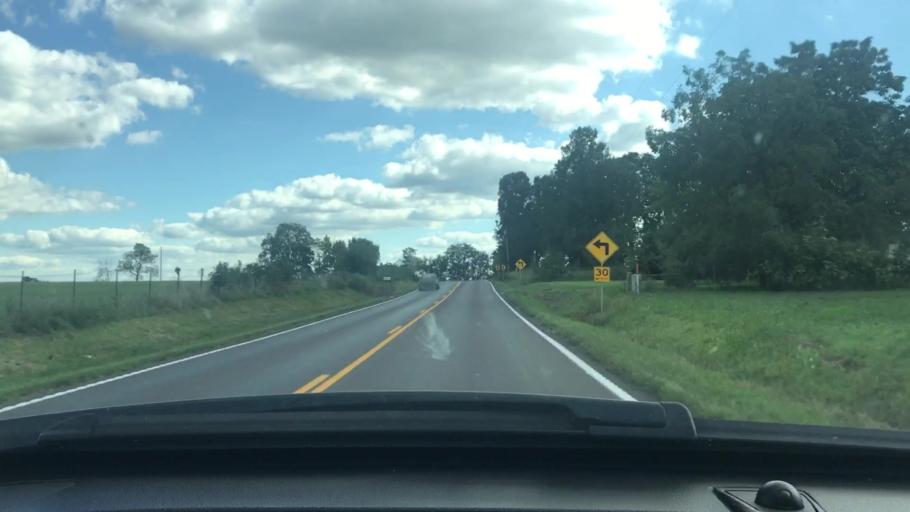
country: US
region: Missouri
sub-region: Wright County
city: Mountain Grove
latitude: 37.1674
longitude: -92.2672
